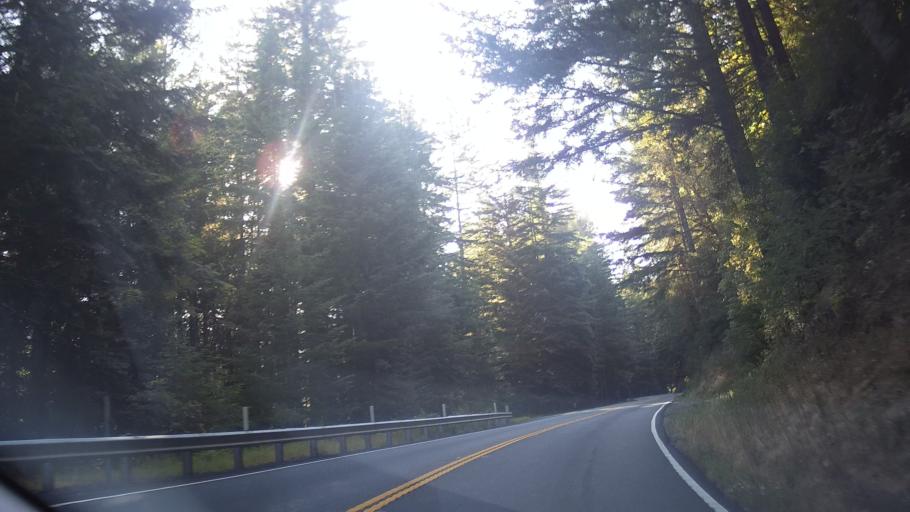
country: US
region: California
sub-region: Mendocino County
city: Fort Bragg
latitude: 39.3628
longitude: -123.6693
